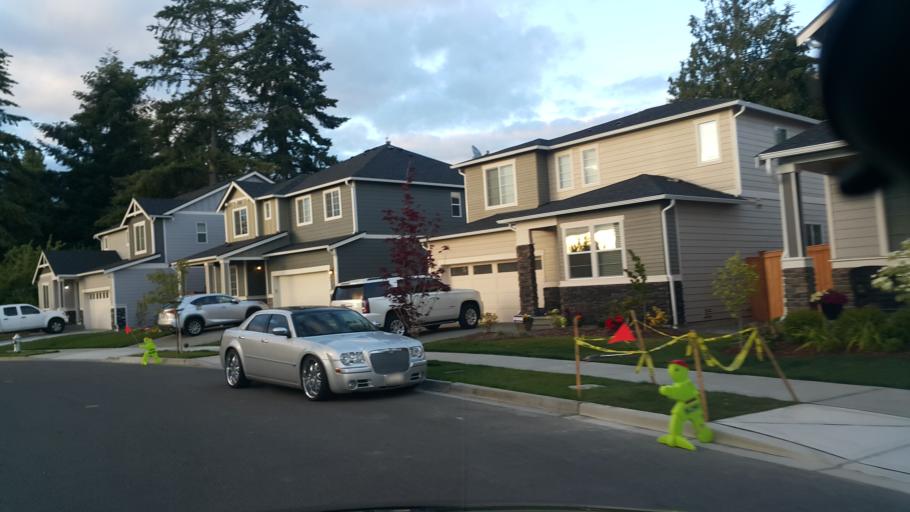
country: US
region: Washington
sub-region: Pierce County
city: University Place
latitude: 47.2159
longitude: -122.5431
